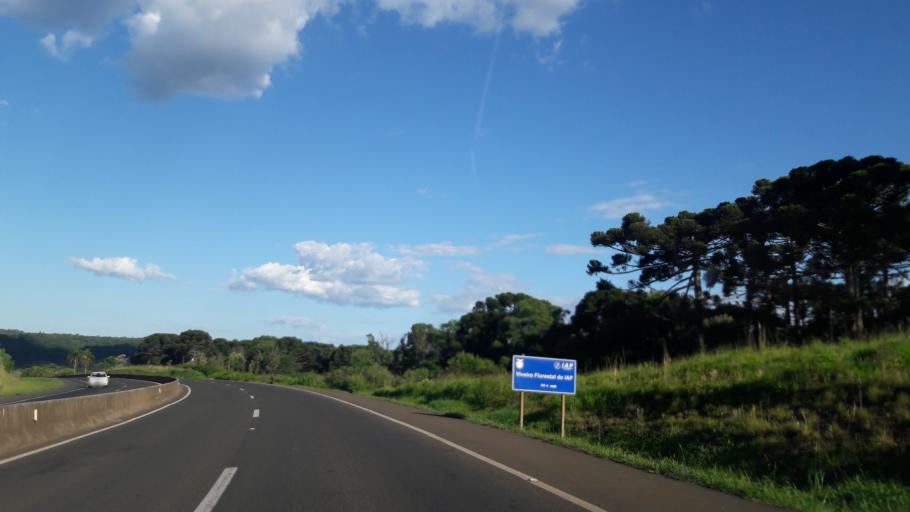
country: BR
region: Parana
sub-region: Guarapuava
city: Guarapuava
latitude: -25.3405
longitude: -51.4239
